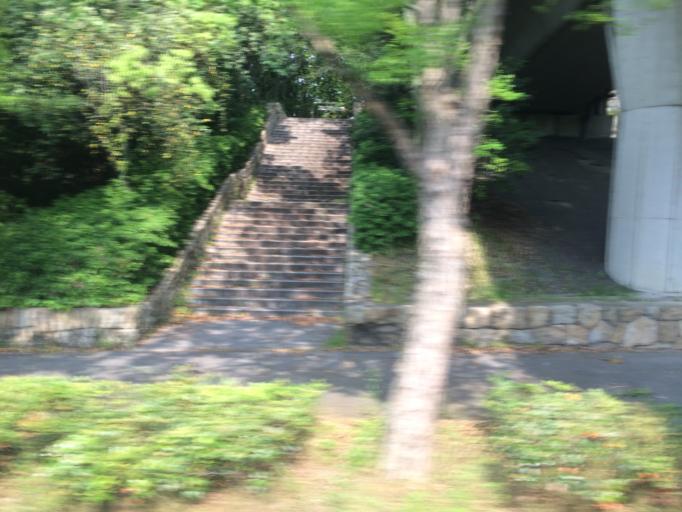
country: JP
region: Hyogo
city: Ashiya
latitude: 34.6937
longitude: 135.2733
